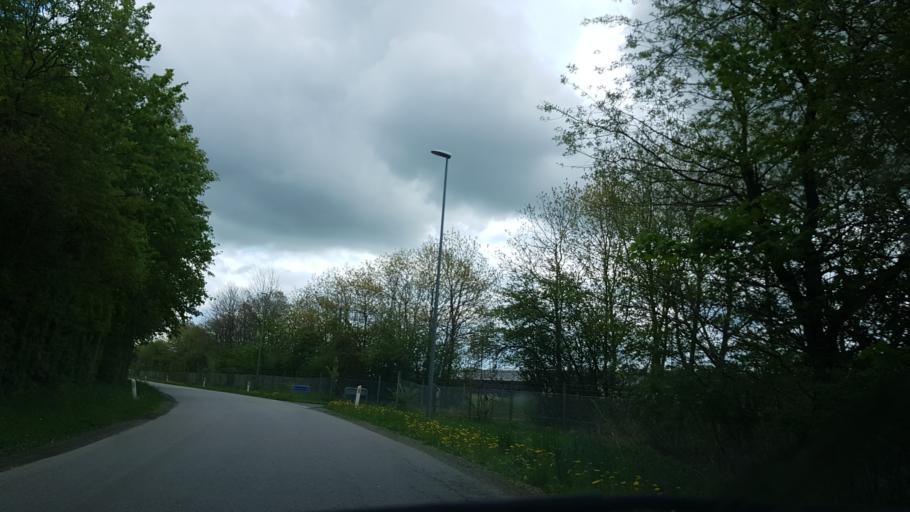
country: DK
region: South Denmark
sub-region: Haderslev Kommune
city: Vojens
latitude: 55.2356
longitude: 9.2645
